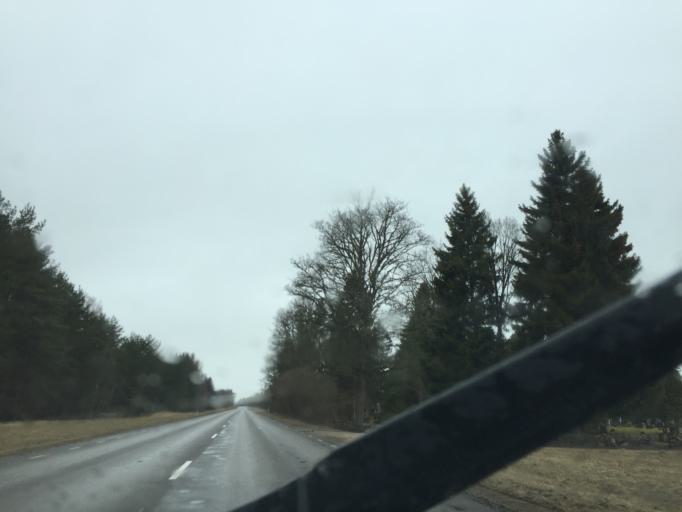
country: EE
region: Laeaene
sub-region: Ridala Parish
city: Uuemoisa
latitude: 58.8737
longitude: 23.6140
